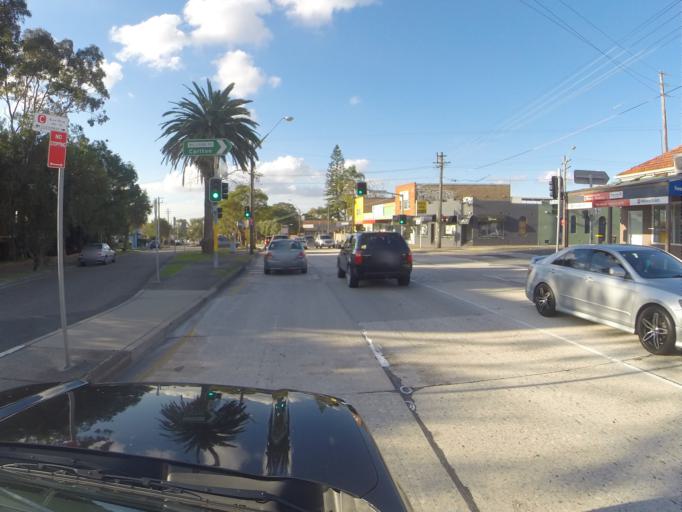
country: AU
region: New South Wales
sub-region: Rockdale
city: Bexley
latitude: -33.9602
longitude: 151.1169
